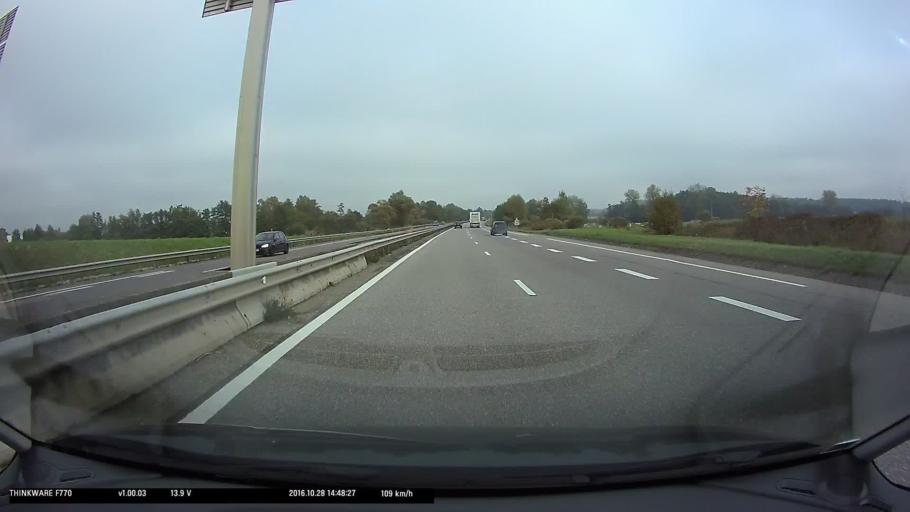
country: FR
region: Lorraine
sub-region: Departement de la Moselle
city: Reding
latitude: 48.7362
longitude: 7.0858
